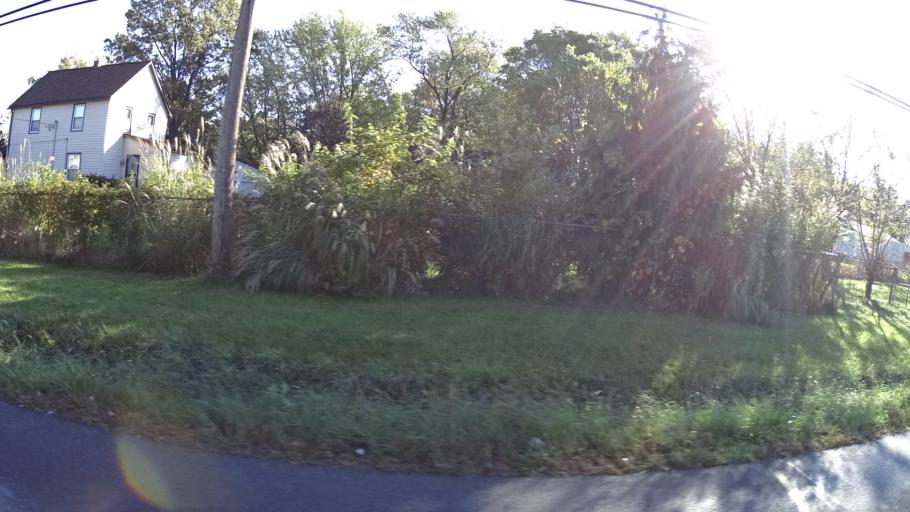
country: US
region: Ohio
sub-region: Lorain County
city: Lorain
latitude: 41.4328
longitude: -82.1575
